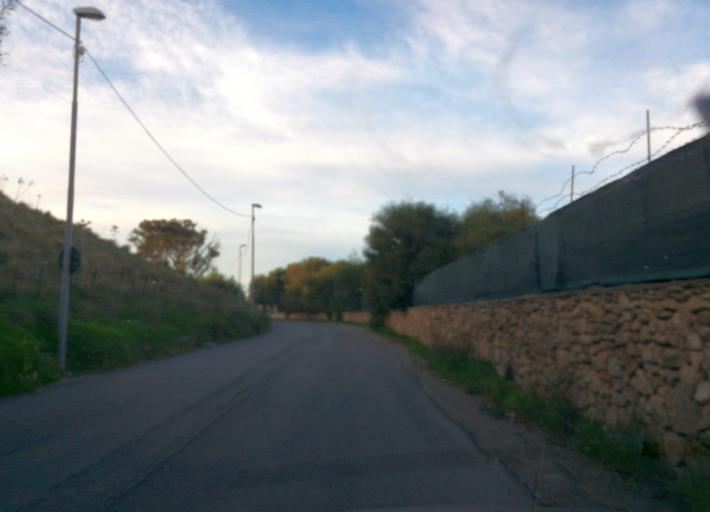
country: IT
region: Calabria
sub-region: Provincia di Crotone
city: Crotone
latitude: 39.0473
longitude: 17.1454
